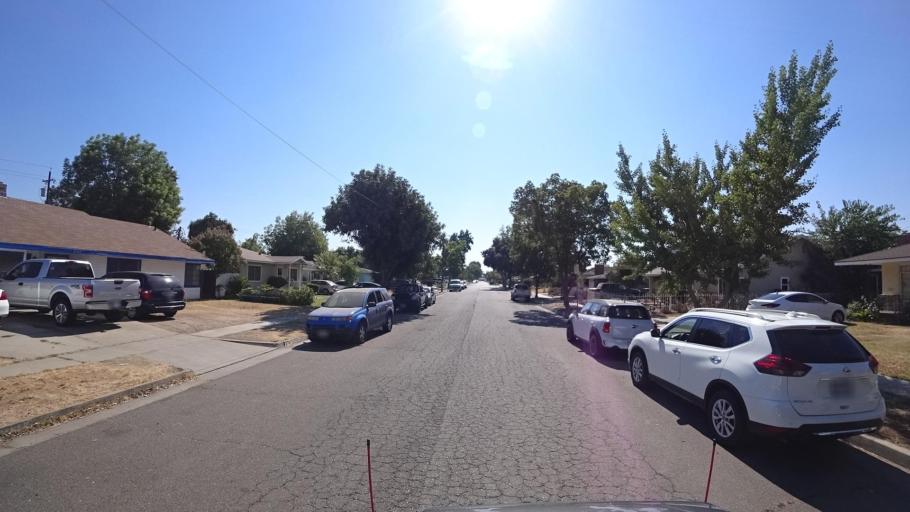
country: US
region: California
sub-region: Fresno County
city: Fresno
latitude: 36.7750
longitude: -119.7784
